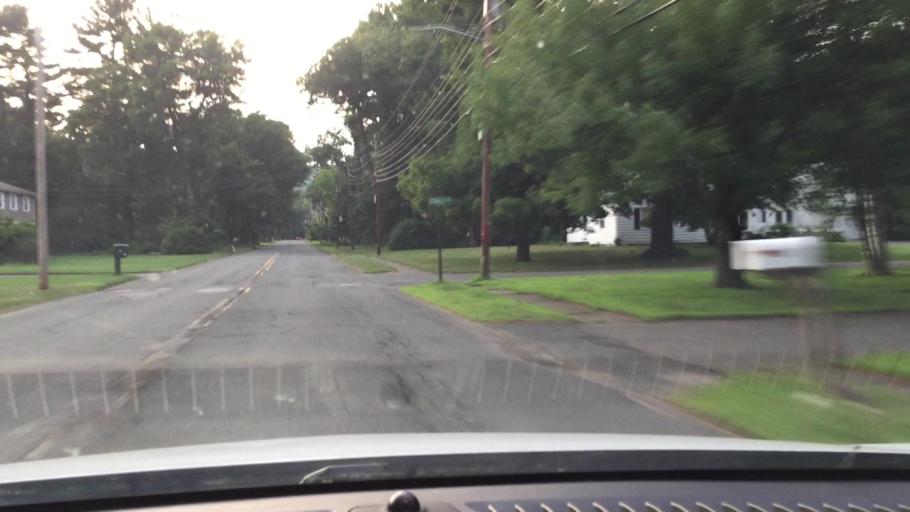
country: US
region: Massachusetts
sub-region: Hampden County
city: Westfield
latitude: 42.1359
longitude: -72.8080
